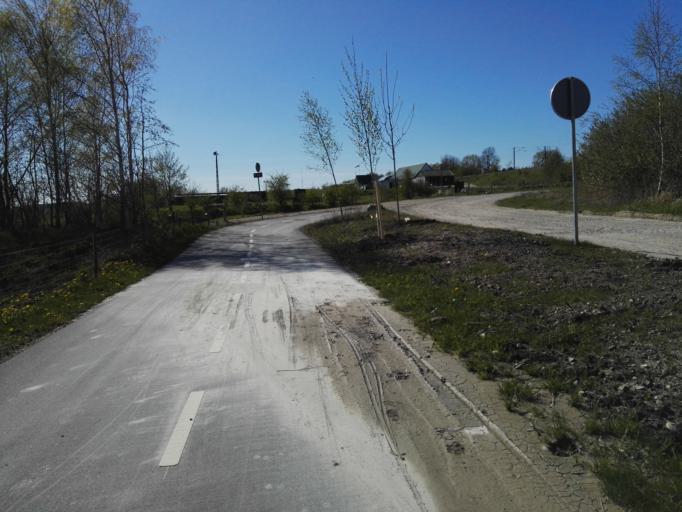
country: DK
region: Capital Region
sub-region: Egedal Kommune
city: Smorumnedre
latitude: 55.7513
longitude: 12.2844
